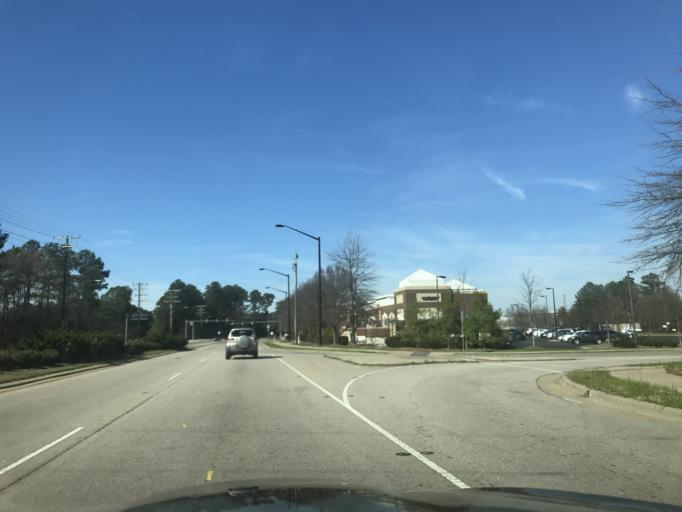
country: US
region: North Carolina
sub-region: Wake County
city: Morrisville
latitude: 35.8667
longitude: -78.8490
